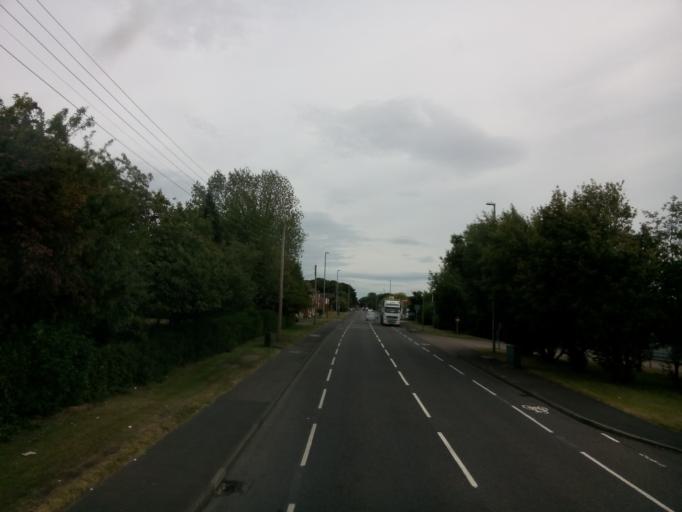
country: GB
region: England
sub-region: County Durham
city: Chester-le-Street
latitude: 54.8818
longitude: -1.5759
